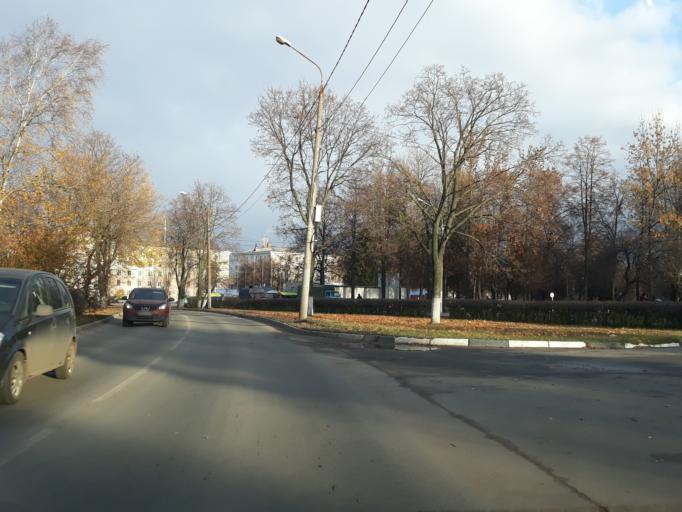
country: RU
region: Nizjnij Novgorod
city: Neklyudovo
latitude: 56.3446
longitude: 43.8604
